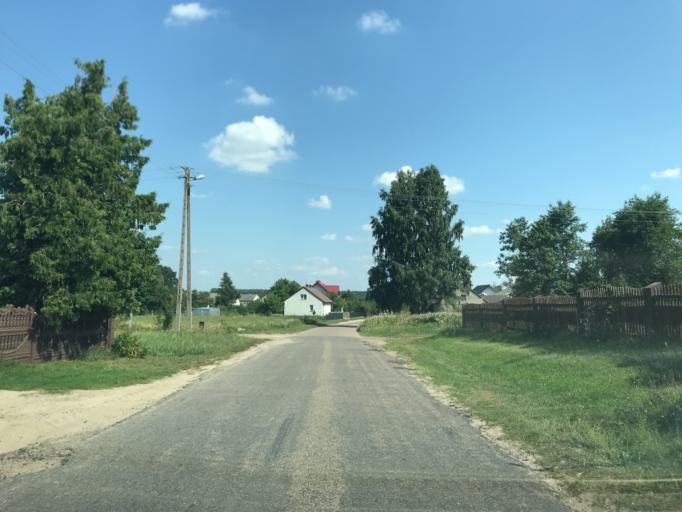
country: PL
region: Masovian Voivodeship
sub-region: Powiat zurominski
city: Zuromin
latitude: 53.1529
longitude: 19.9301
